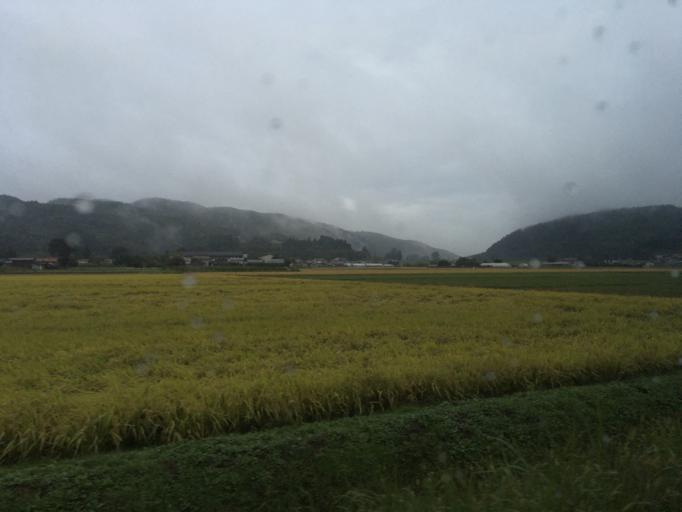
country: JP
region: Iwate
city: Ichinoseki
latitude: 38.8359
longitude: 141.2531
